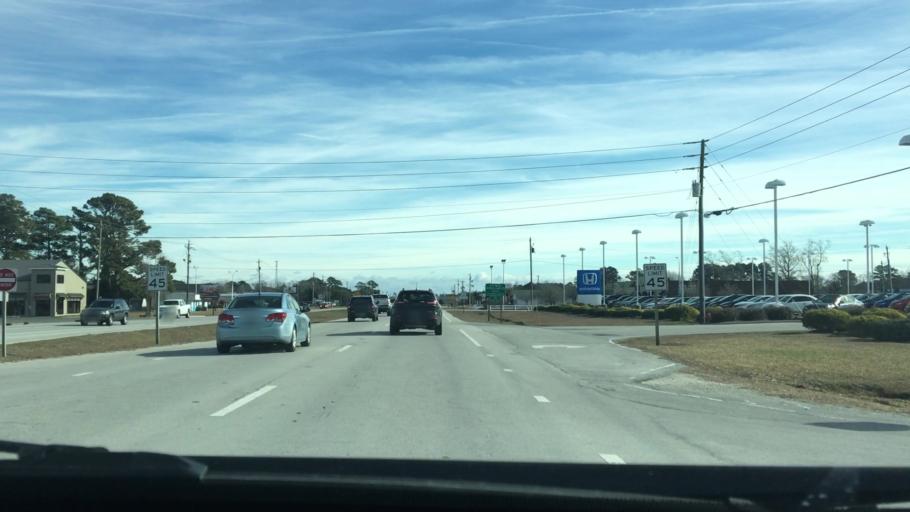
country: US
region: North Carolina
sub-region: Carteret County
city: Pine Knoll Shores
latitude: 34.7422
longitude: -76.8207
